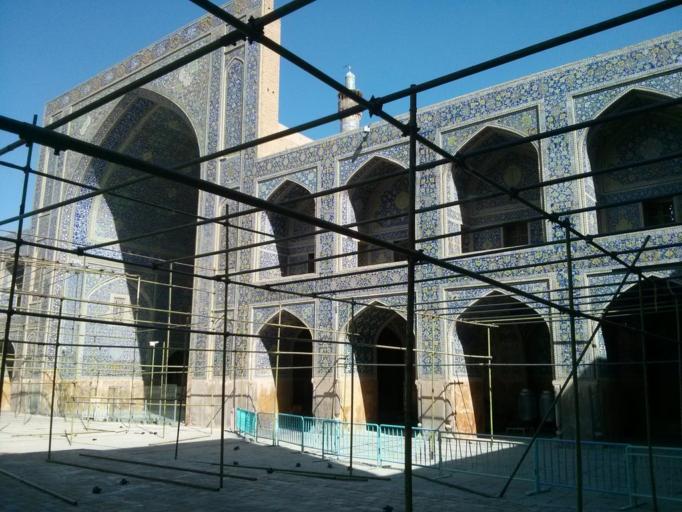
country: IR
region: Isfahan
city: Isfahan
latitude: 32.6543
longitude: 51.6780
